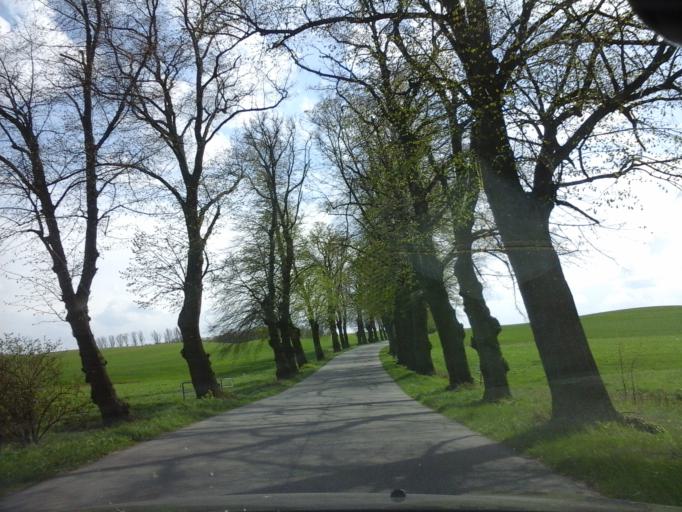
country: PL
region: West Pomeranian Voivodeship
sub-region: Powiat choszczenski
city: Pelczyce
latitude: 53.0929
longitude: 15.3507
